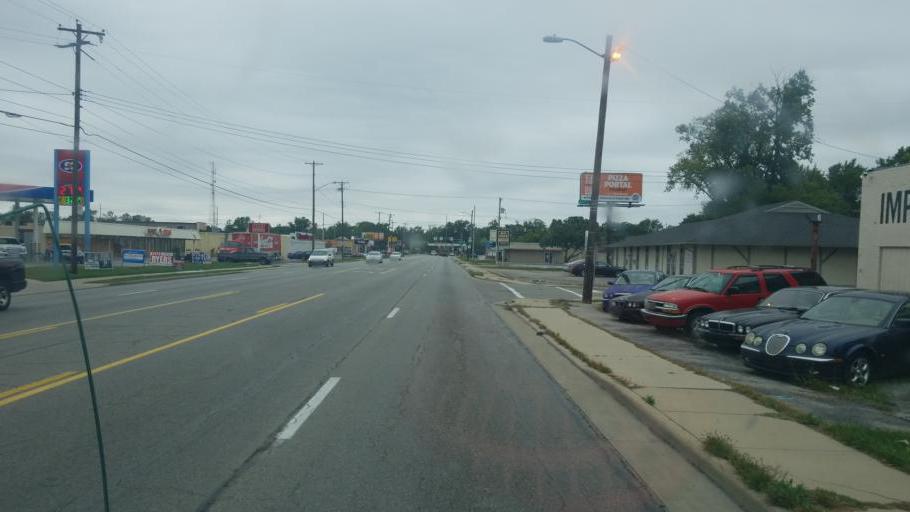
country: US
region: Ohio
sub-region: Lucas County
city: Ottawa Hills
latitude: 41.6499
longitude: -83.6646
